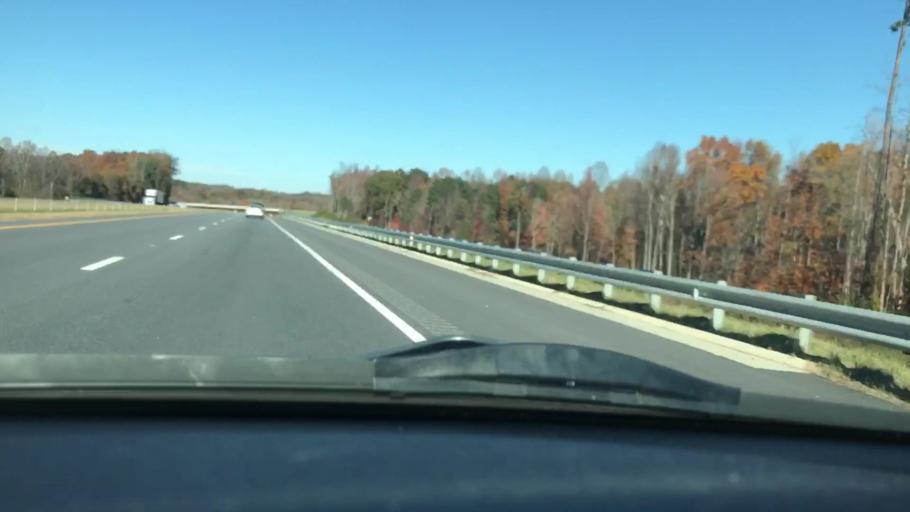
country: US
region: North Carolina
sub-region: Guilford County
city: Summerfield
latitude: 36.2196
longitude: -79.9152
